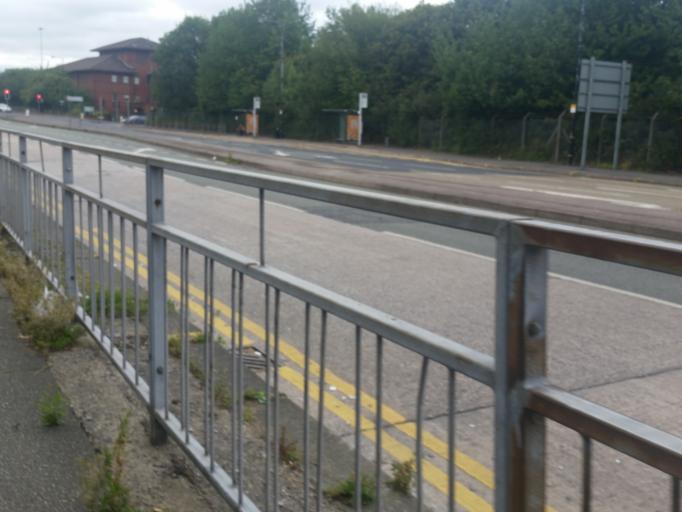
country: GB
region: England
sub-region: Manchester
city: Hulme
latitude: 53.4625
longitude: -2.2761
